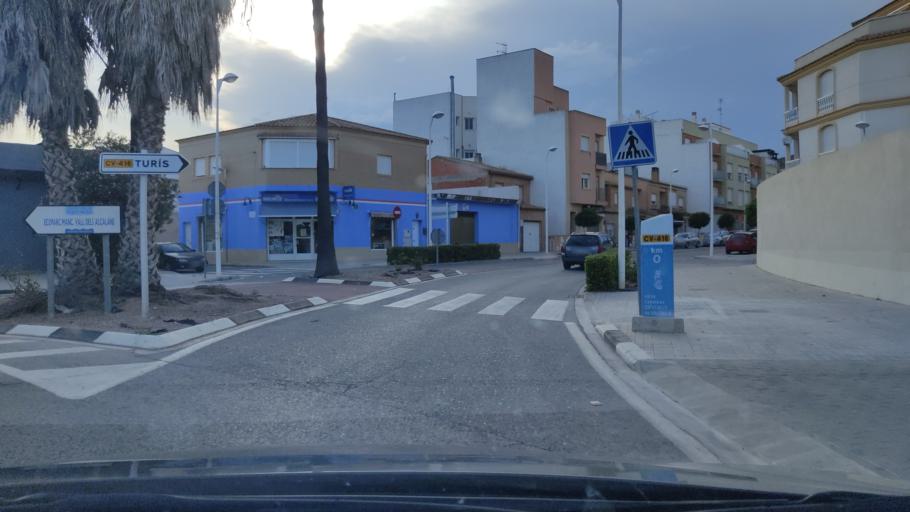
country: ES
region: Valencia
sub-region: Provincia de Valencia
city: Monserrat
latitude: 39.3575
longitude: -0.5972
